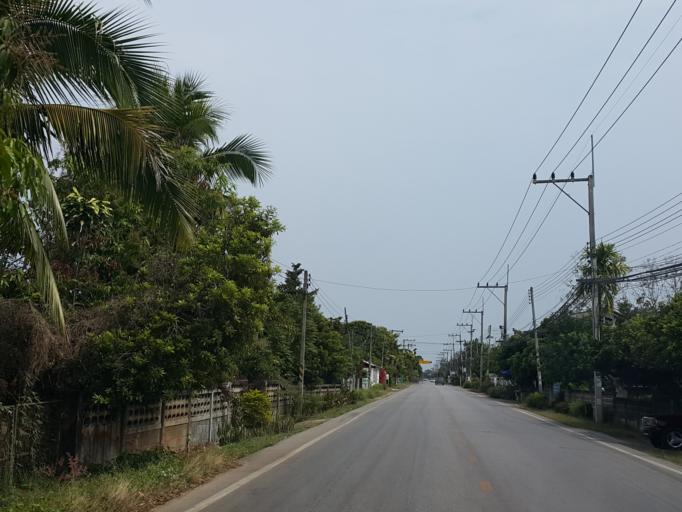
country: TH
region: Lampang
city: Ko Kha
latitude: 18.1682
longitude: 99.3859
